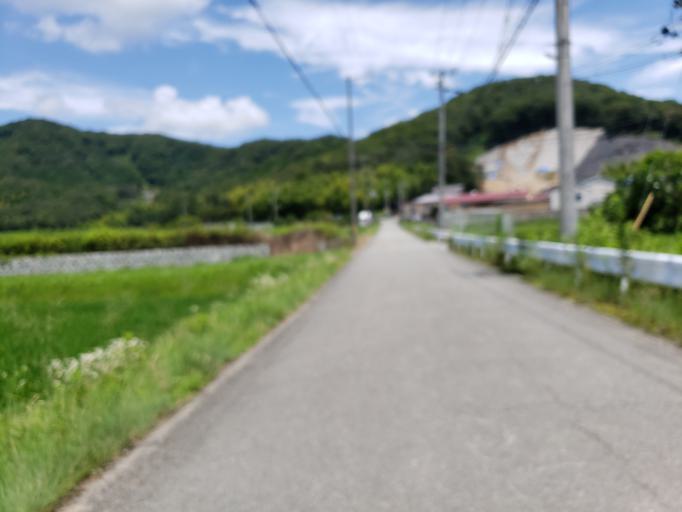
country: JP
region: Hyogo
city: Kakogawacho-honmachi
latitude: 34.8254
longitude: 134.8119
